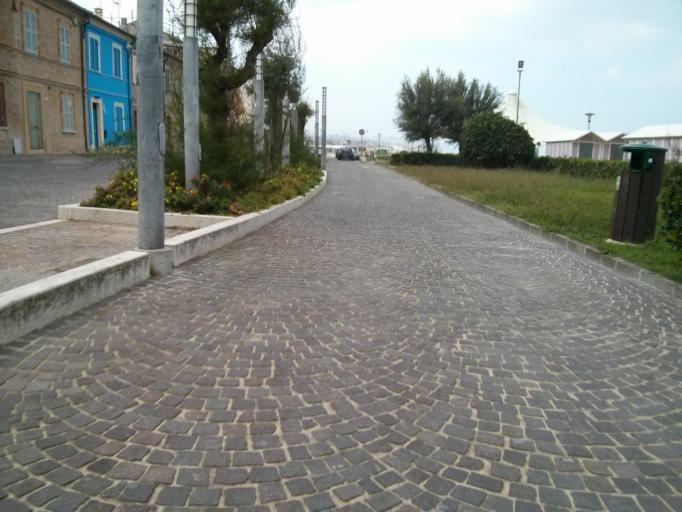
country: IT
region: The Marches
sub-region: Provincia di Pesaro e Urbino
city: Fano
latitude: 43.8518
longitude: 13.0102
